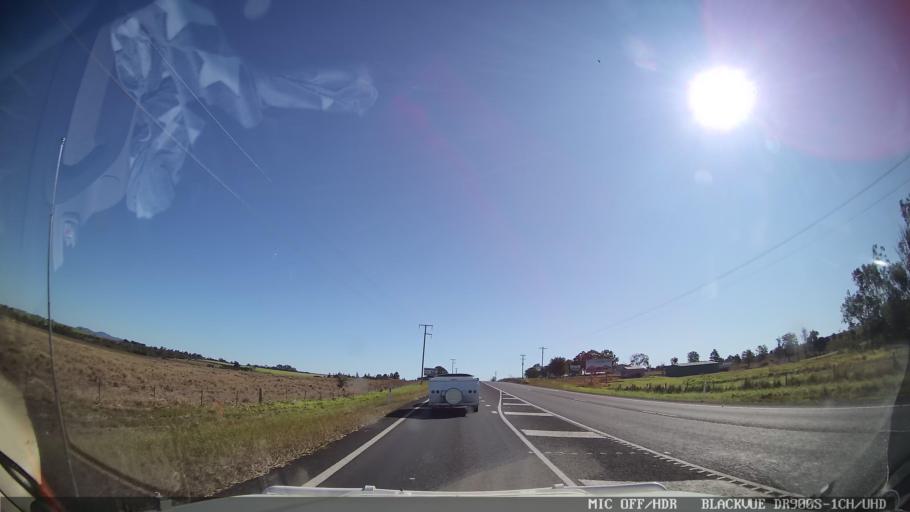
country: AU
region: Queensland
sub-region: Bundaberg
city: Childers
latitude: -25.2478
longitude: 152.3288
